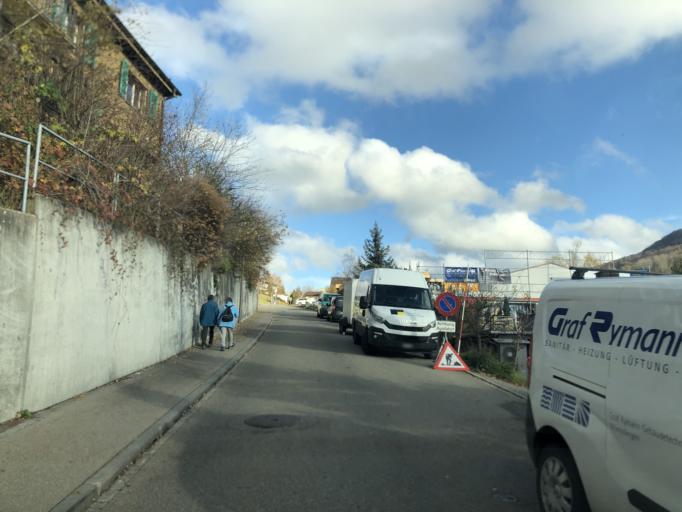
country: CH
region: Aargau
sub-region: Bezirk Baden
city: Wettingen
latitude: 47.4839
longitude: 8.3254
